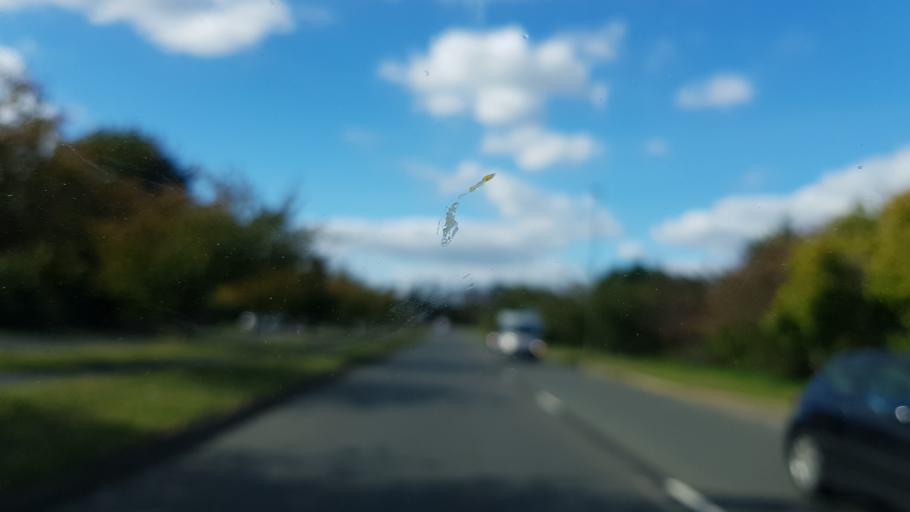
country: GB
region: England
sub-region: Surrey
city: Milford
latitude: 51.1693
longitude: -0.6493
